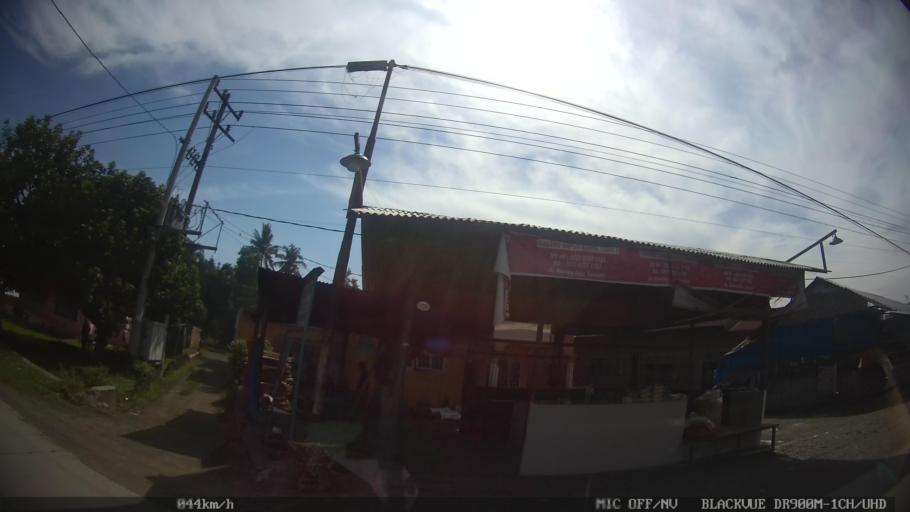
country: ID
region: North Sumatra
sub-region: Kabupaten Langkat
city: Stabat
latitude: 3.7202
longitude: 98.5031
